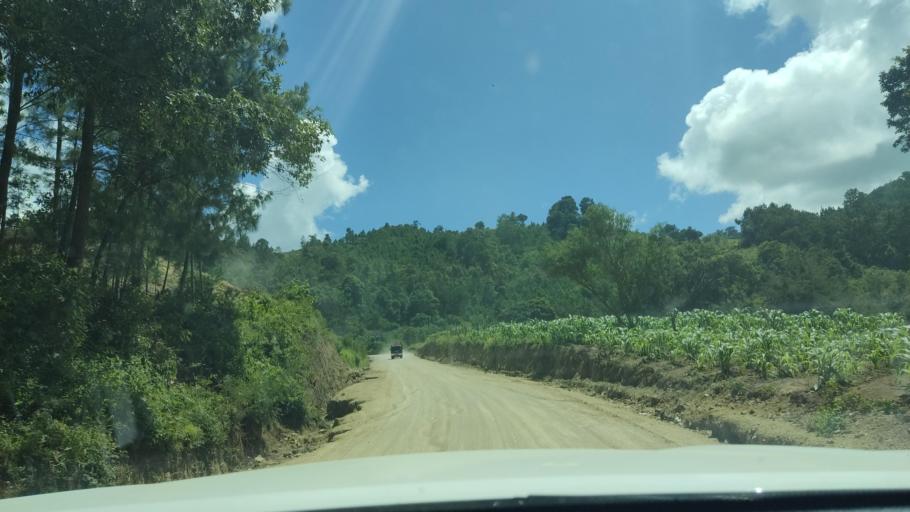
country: GT
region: Chimaltenango
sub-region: Municipio de San Juan Comalapa
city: Comalapa
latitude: 14.7607
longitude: -90.8860
